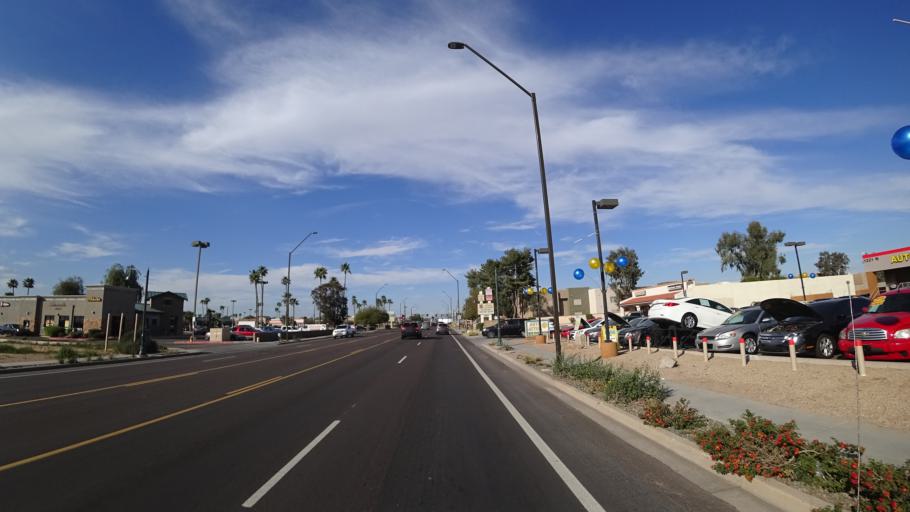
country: US
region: Arizona
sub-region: Maricopa County
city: Avondale
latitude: 33.4474
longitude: -112.3410
